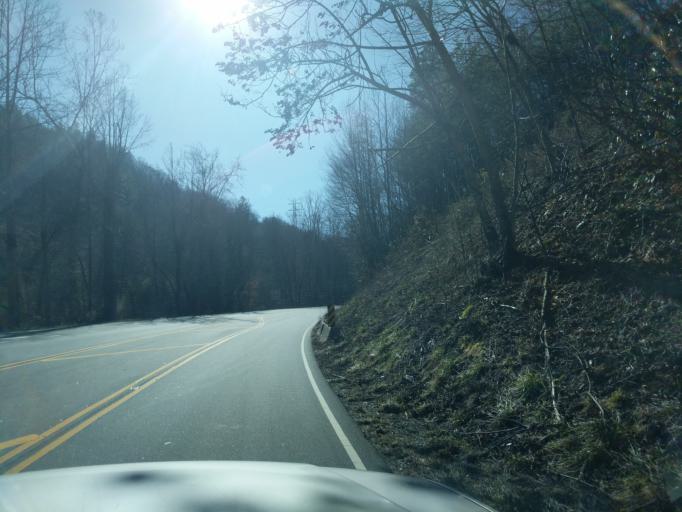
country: US
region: North Carolina
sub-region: Graham County
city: Robbinsville
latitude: 35.2736
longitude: -83.6825
